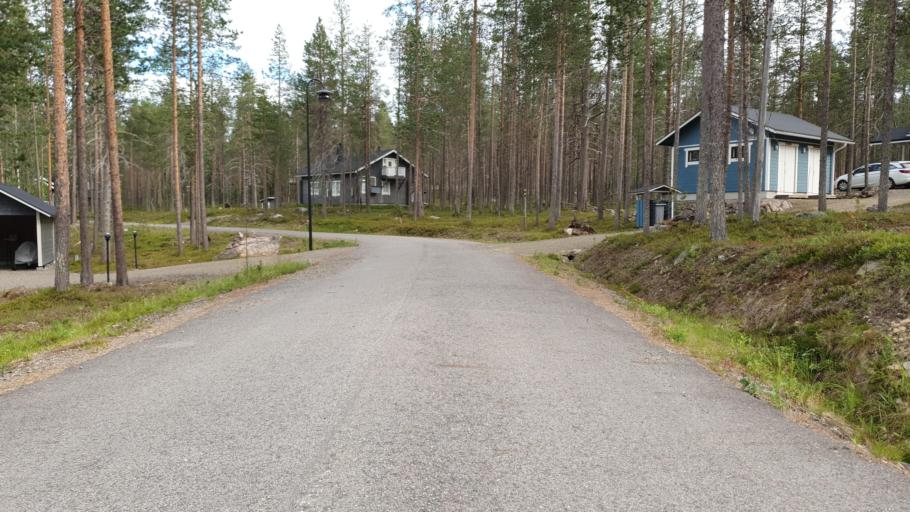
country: FI
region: Lapland
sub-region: Tunturi-Lappi
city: Kolari
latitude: 67.5910
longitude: 24.1251
